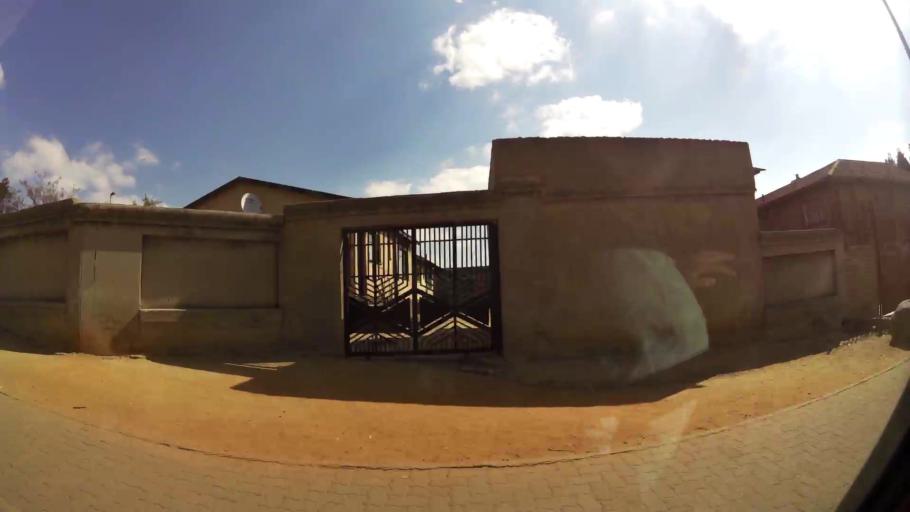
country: ZA
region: Gauteng
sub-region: Ekurhuleni Metropolitan Municipality
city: Tembisa
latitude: -26.0127
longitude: 28.1993
